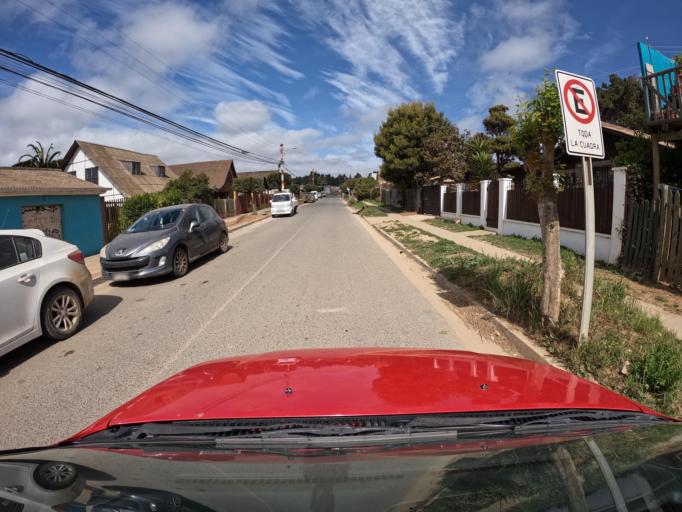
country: CL
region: O'Higgins
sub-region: Provincia de Colchagua
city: Santa Cruz
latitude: -34.3921
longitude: -72.0171
